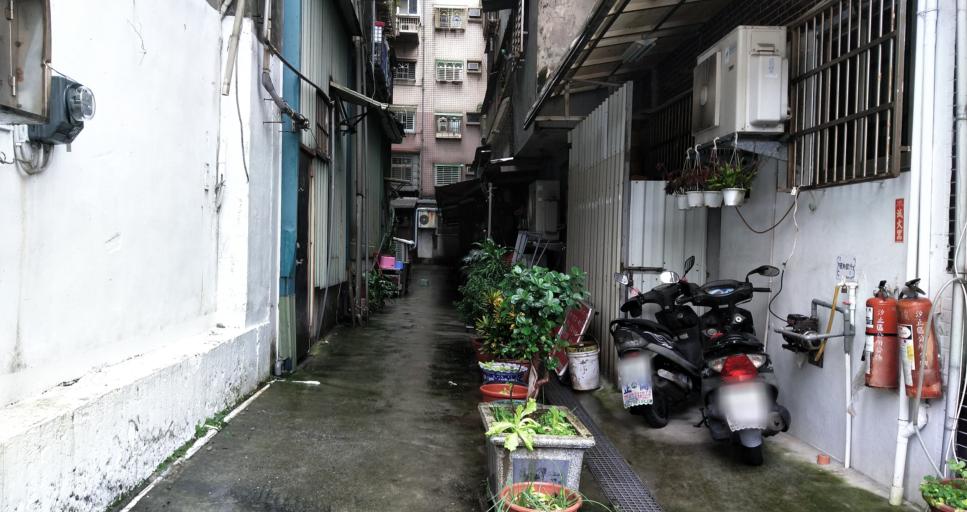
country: TW
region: Taiwan
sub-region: Keelung
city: Keelung
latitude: 25.0710
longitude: 121.6633
